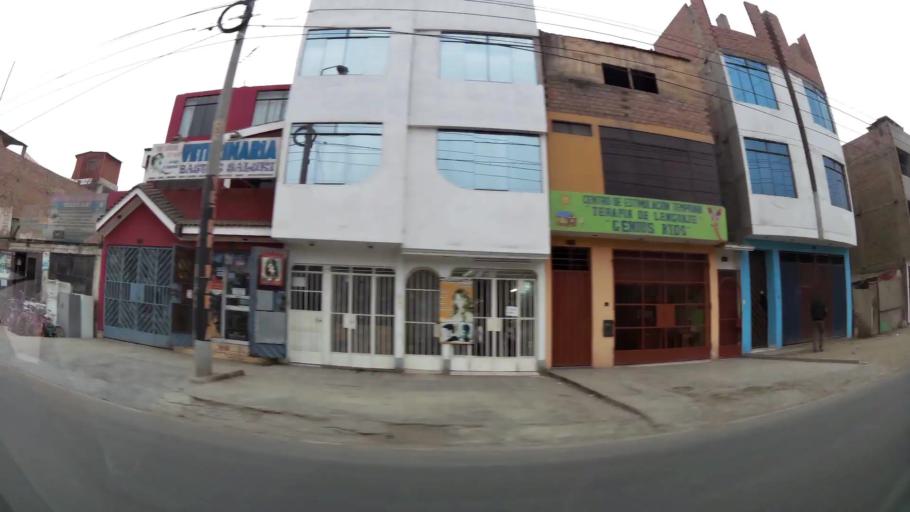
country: PE
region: Lima
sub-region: Lima
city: Urb. Santo Domingo
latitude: -11.8853
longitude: -77.0349
